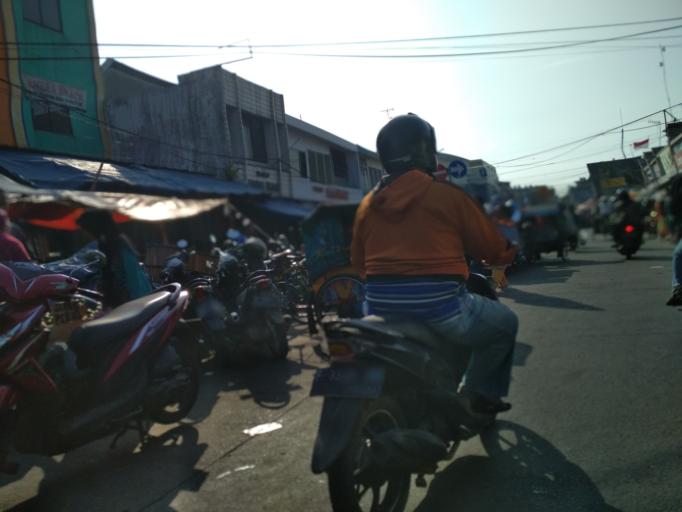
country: ID
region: West Java
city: Bogor
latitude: -6.5906
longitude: 106.7905
